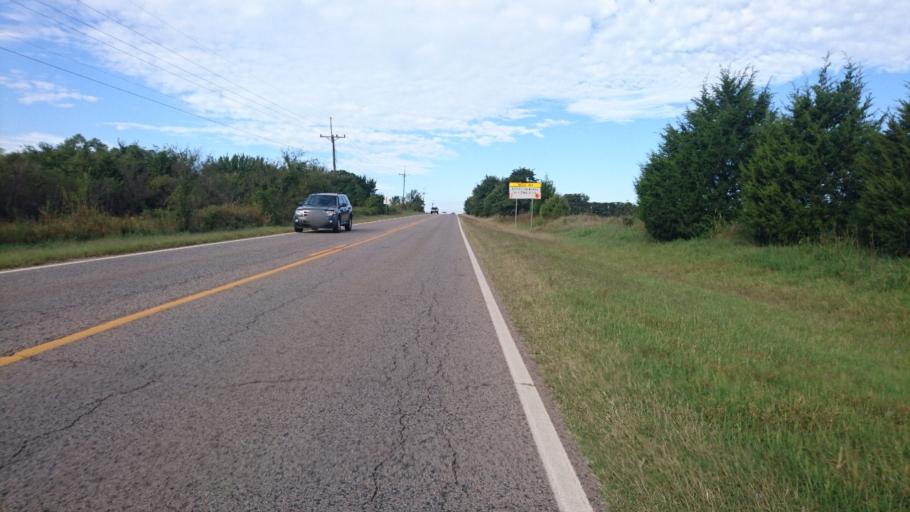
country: US
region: Oklahoma
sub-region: Lincoln County
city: Chandler
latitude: 35.6811
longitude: -97.0224
